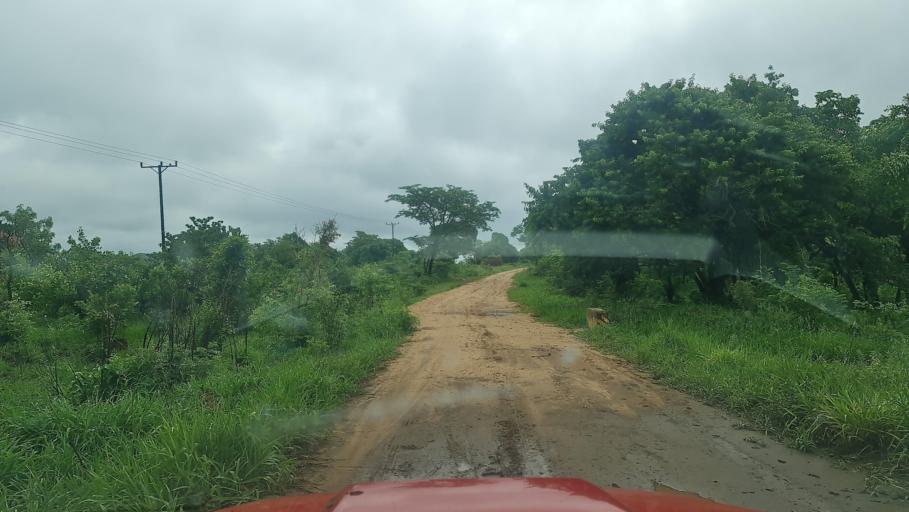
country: MW
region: Southern Region
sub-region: Nsanje District
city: Nsanje
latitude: -17.1927
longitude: 35.8516
